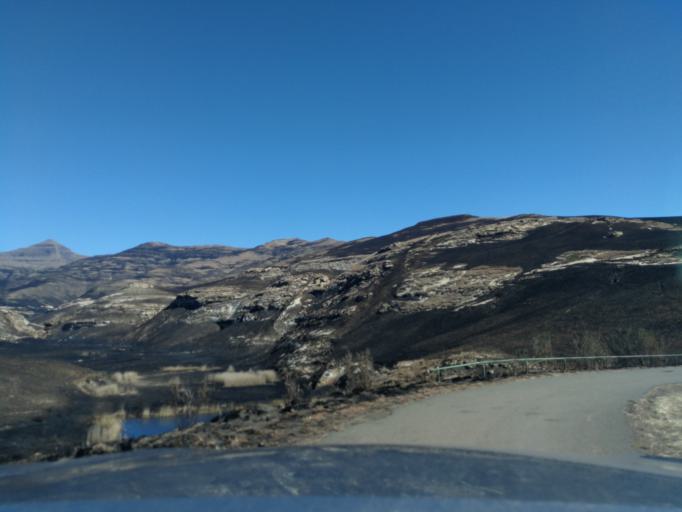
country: ZA
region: Orange Free State
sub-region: Thabo Mofutsanyana District Municipality
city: Phuthaditjhaba
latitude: -28.5138
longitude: 28.6183
